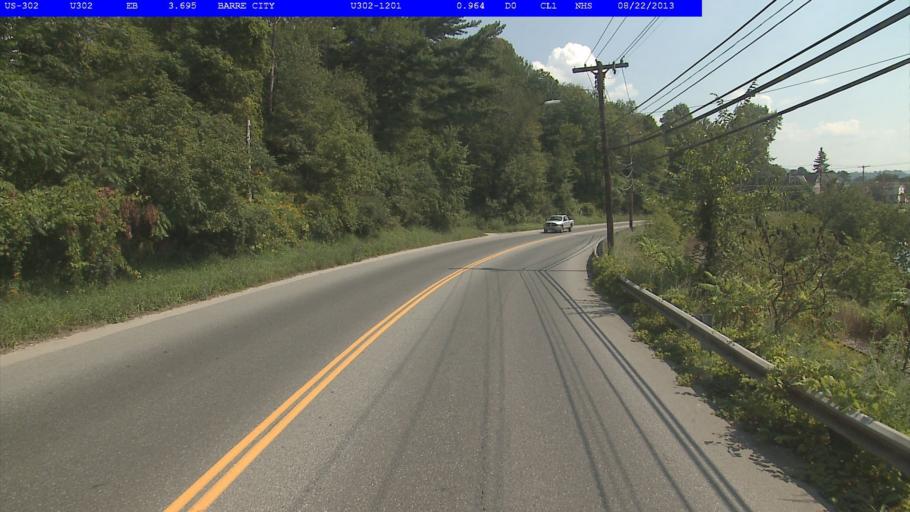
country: US
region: Vermont
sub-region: Washington County
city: Barre
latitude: 44.2109
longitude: -72.5169
